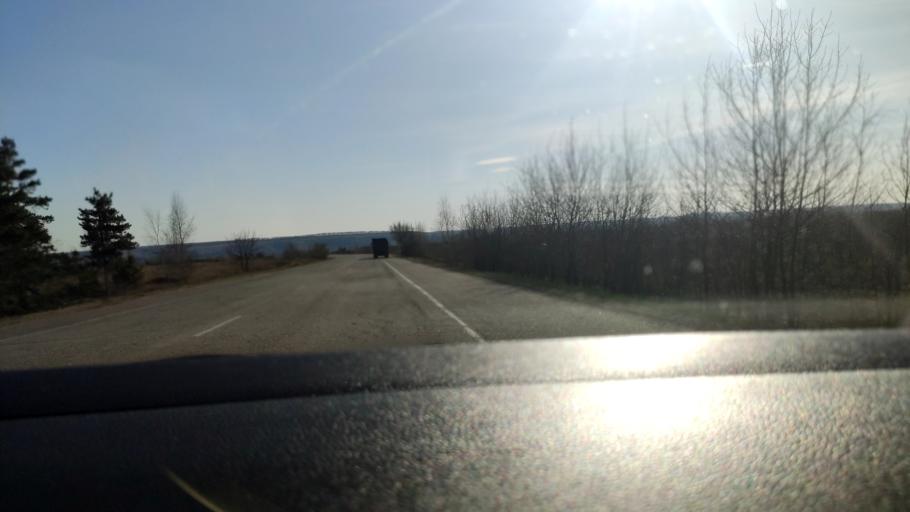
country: RU
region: Voronezj
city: Kolodeznyy
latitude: 51.3590
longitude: 39.1819
